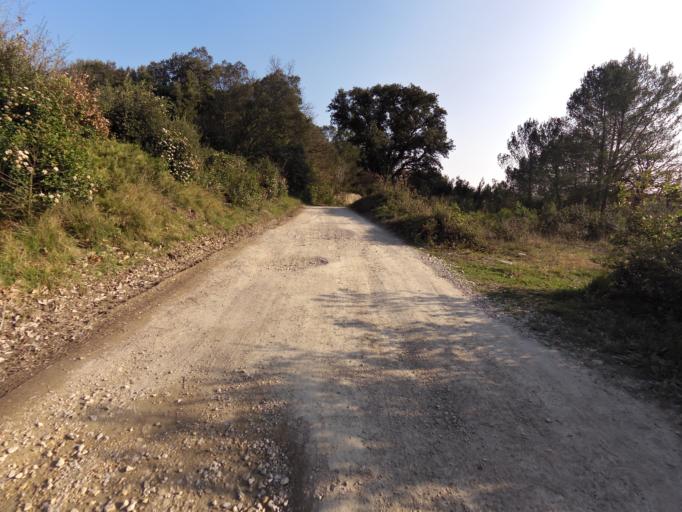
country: FR
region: Languedoc-Roussillon
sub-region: Departement du Gard
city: Aubais
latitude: 43.7419
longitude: 4.1592
